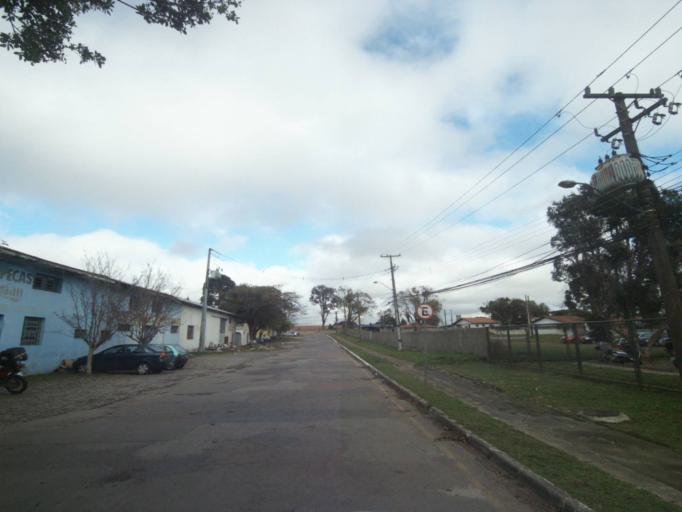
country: BR
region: Parana
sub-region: Sao Jose Dos Pinhais
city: Sao Jose dos Pinhais
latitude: -25.5284
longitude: -49.2997
